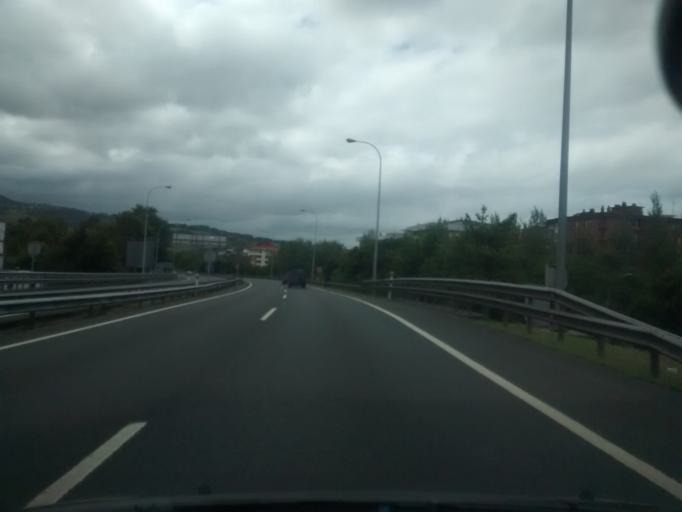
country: ES
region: Basque Country
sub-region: Provincia de Guipuzcoa
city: Zarautz
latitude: 43.2799
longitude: -2.1614
